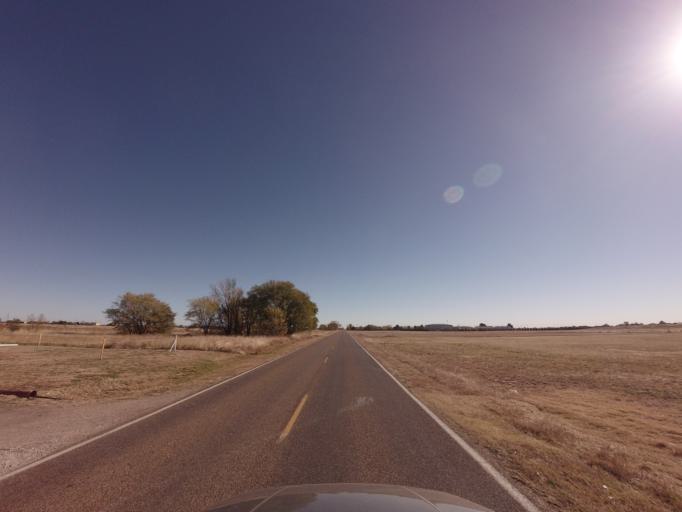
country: US
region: New Mexico
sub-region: Curry County
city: Clovis
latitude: 34.4194
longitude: -103.1665
